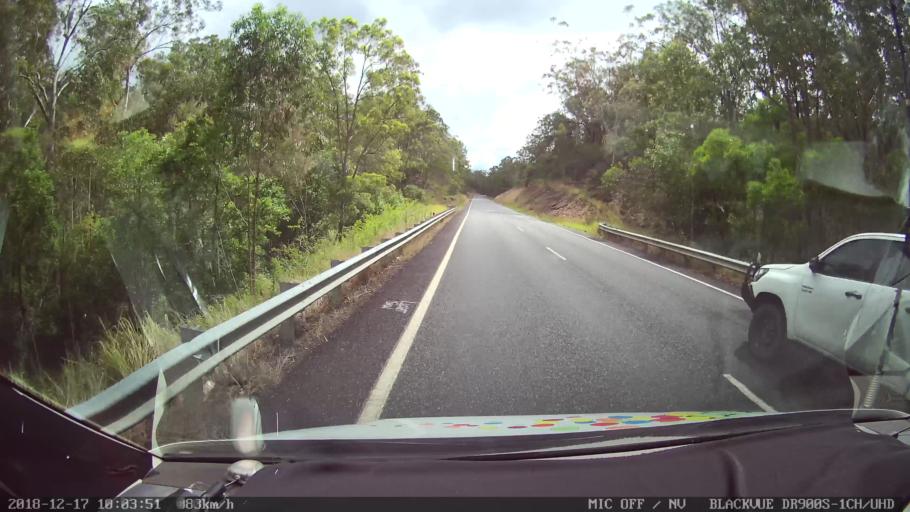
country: AU
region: New South Wales
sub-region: Tenterfield Municipality
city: Carrolls Creek
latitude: -28.8959
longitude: 152.4694
